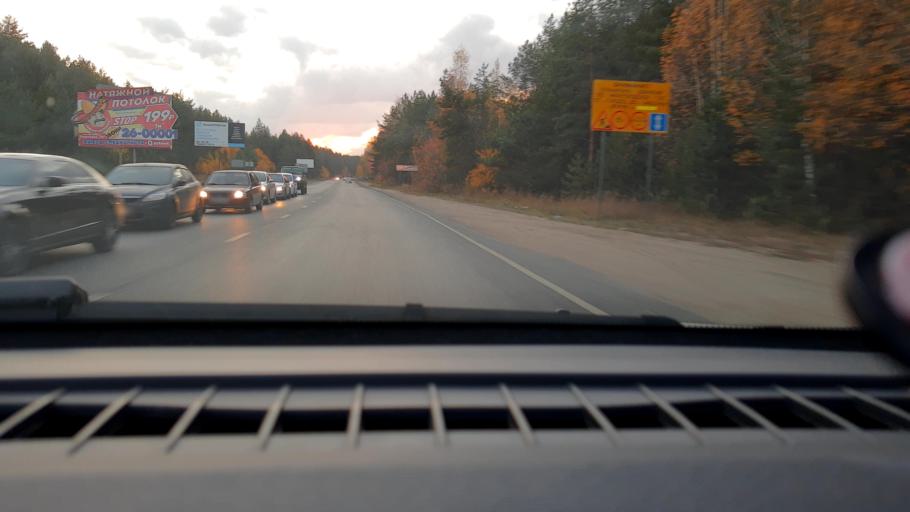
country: RU
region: Nizjnij Novgorod
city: Lukino
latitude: 56.3896
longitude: 43.7318
